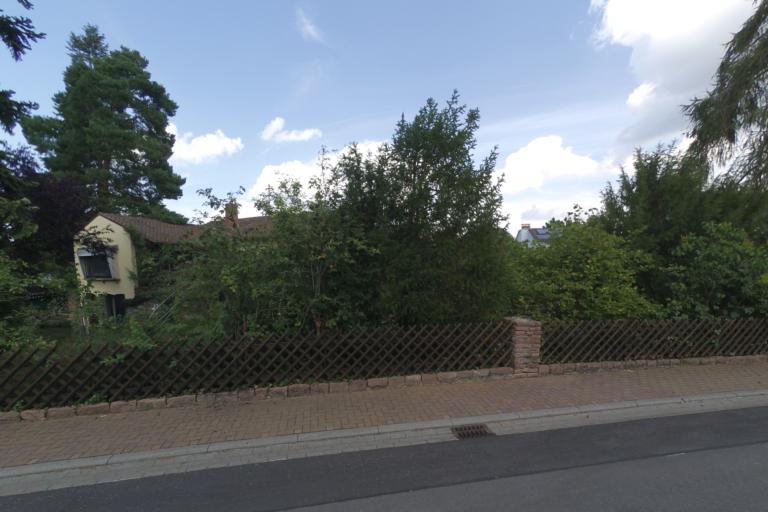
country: DE
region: Rheinland-Pfalz
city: Limburgerhof
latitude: 49.4142
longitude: 8.3861
